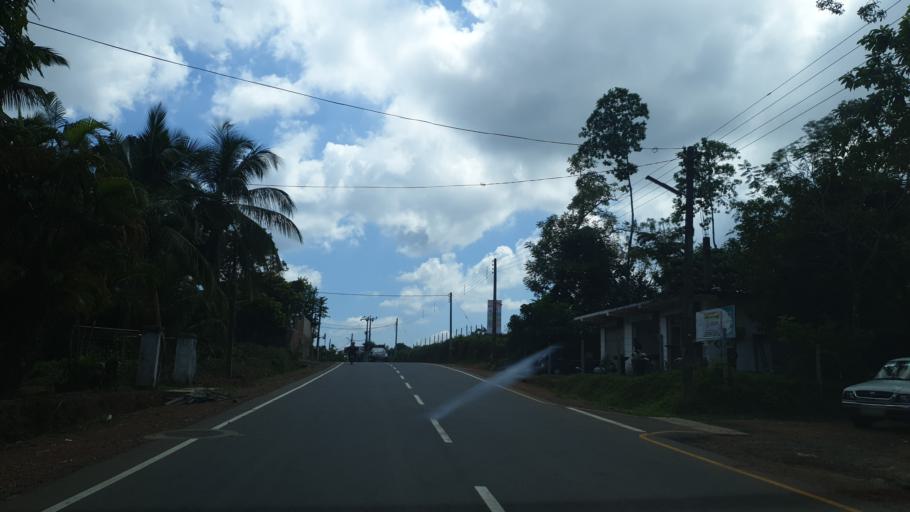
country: LK
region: Western
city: Panadura
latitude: 6.6685
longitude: 79.9463
